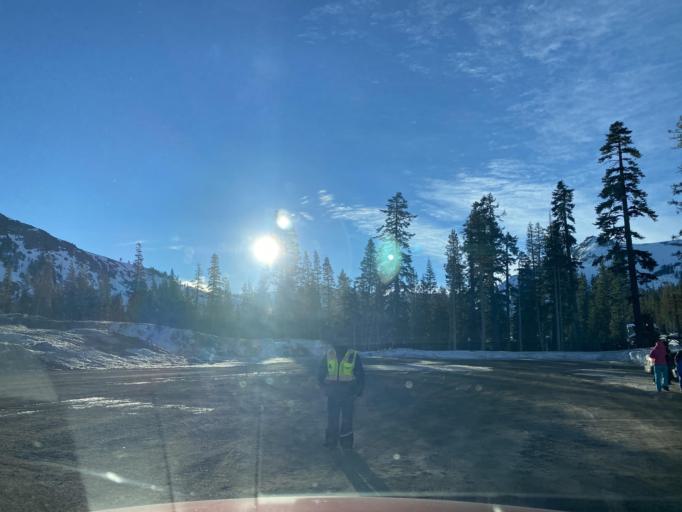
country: US
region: California
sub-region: El Dorado County
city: South Lake Tahoe
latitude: 38.6889
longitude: -120.0730
